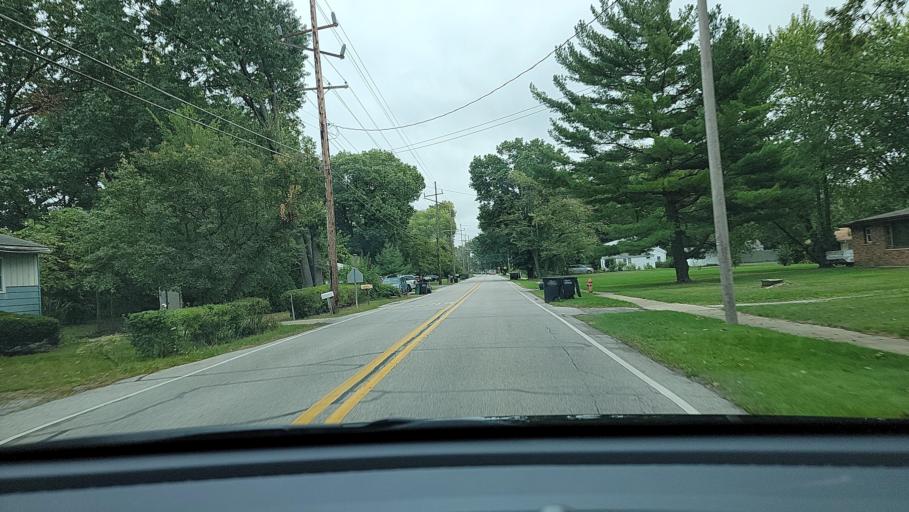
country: US
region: Indiana
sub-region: Porter County
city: Portage
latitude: 41.5717
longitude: -87.1890
